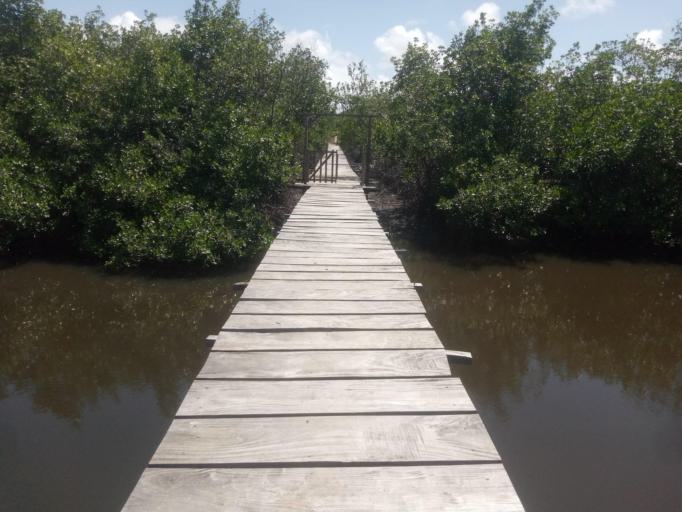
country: GM
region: Western
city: Gunjur
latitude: 13.0408
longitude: -16.7359
